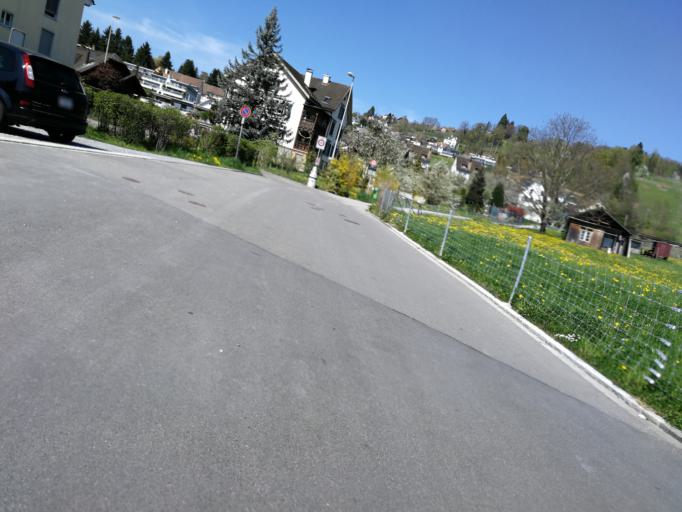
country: CH
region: Zurich
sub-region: Bezirk Meilen
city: Maennedorf / Ausserfeld
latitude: 47.2482
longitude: 8.7085
